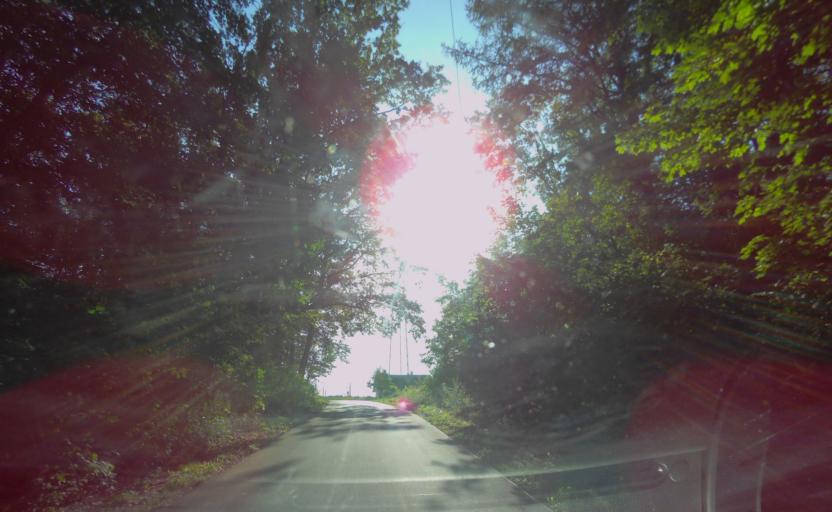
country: PL
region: Subcarpathian Voivodeship
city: Nowa Sarzyna
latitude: 50.2958
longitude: 22.3744
